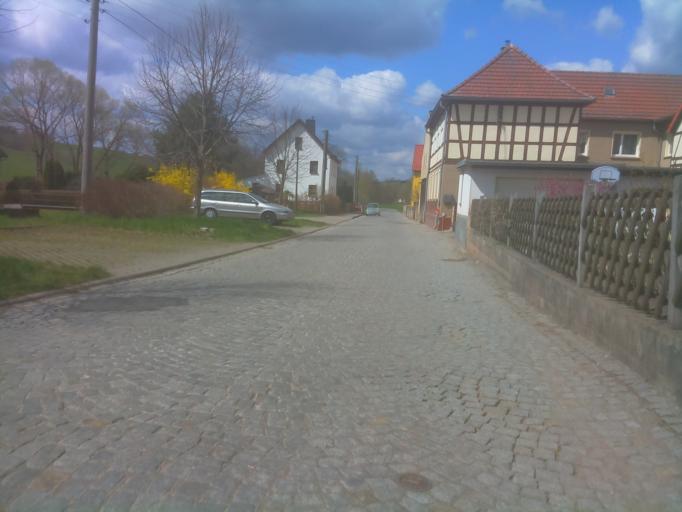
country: DE
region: Thuringia
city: Kleinebersdorf
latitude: 50.8183
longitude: 11.8361
